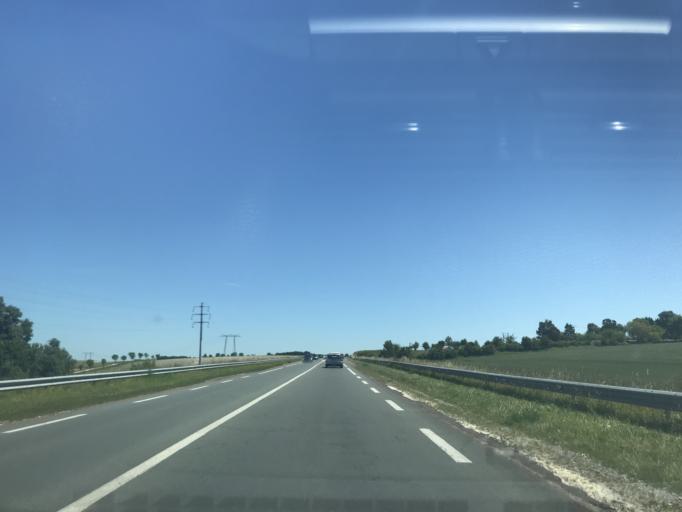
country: FR
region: Poitou-Charentes
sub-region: Departement de la Charente-Maritime
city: Saint-Georges-de-Didonne
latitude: 45.6137
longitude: -0.9840
